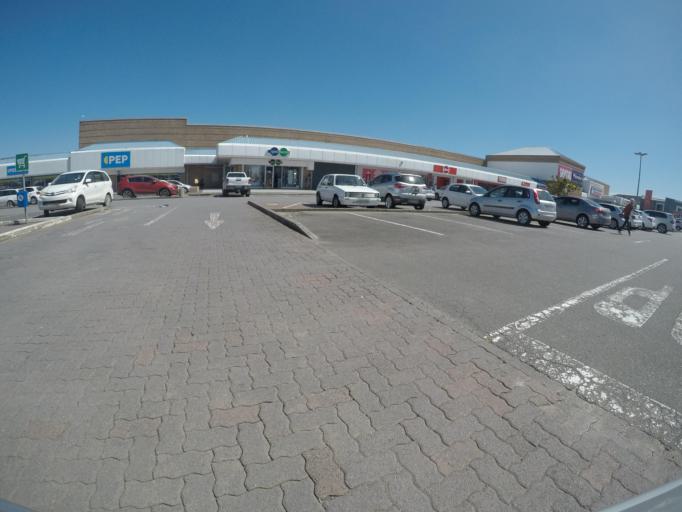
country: ZA
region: Eastern Cape
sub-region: Buffalo City Metropolitan Municipality
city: East London
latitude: -32.9551
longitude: 27.9324
